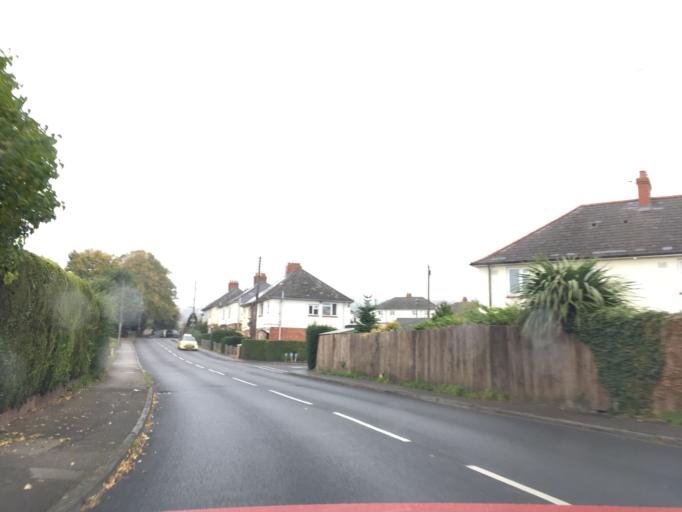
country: GB
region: England
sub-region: Gloucestershire
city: Stonehouse
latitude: 51.7455
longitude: -2.2438
